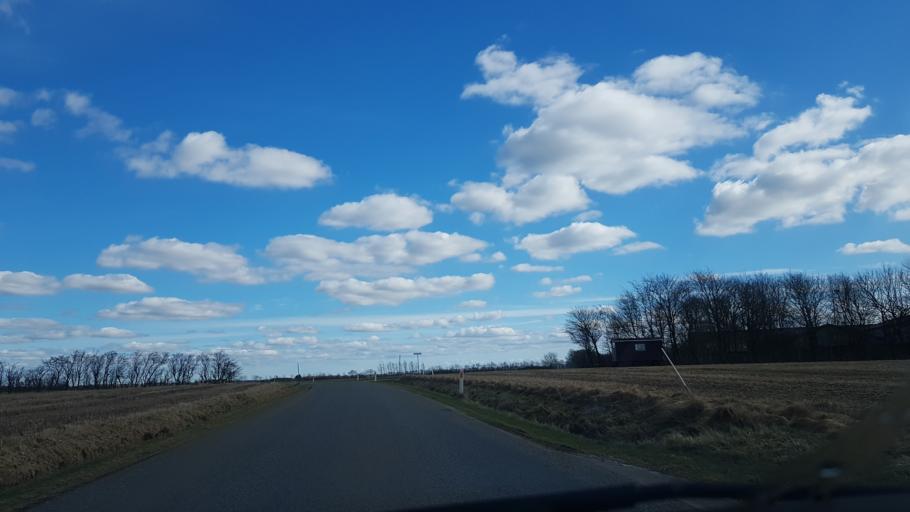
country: DK
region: South Denmark
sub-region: Vejen Kommune
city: Brorup
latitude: 55.4056
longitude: 8.9478
